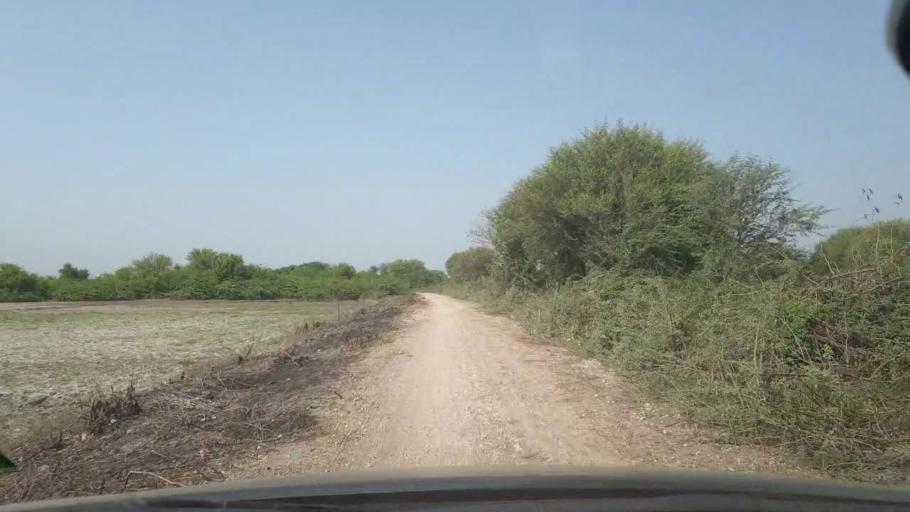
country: PK
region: Sindh
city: Naukot
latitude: 24.7998
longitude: 69.2410
